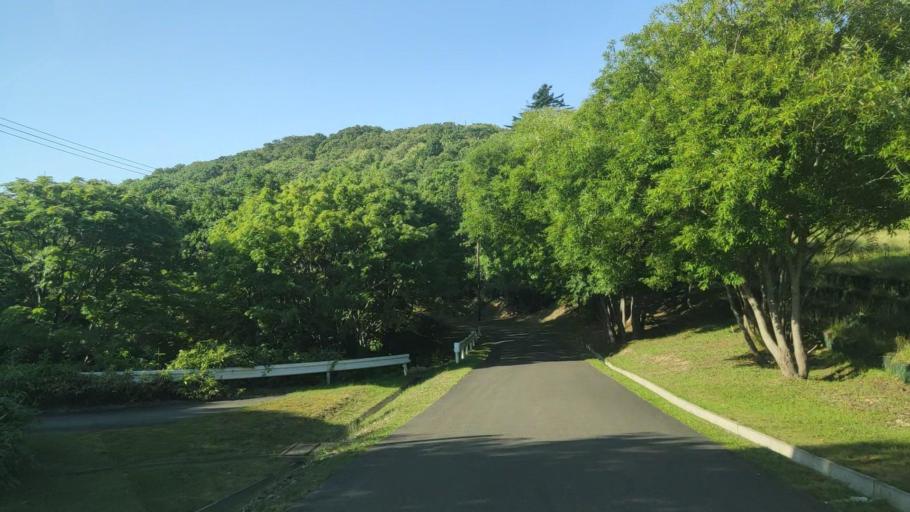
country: JP
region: Hokkaido
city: Wakkanai
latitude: 45.4157
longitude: 141.6675
